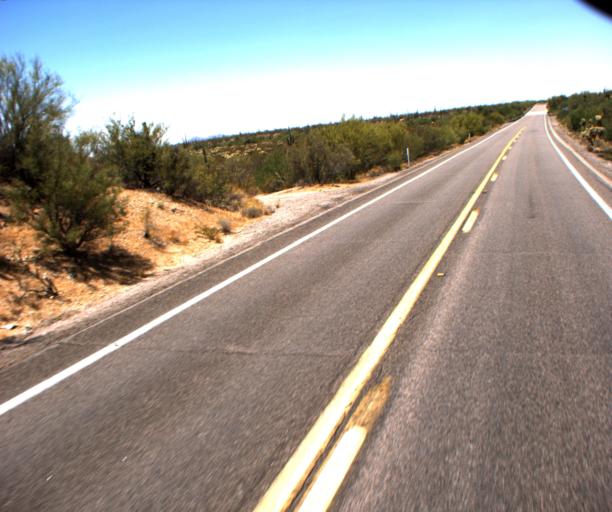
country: US
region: Arizona
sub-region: Pima County
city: Marana
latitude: 32.7714
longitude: -111.1592
